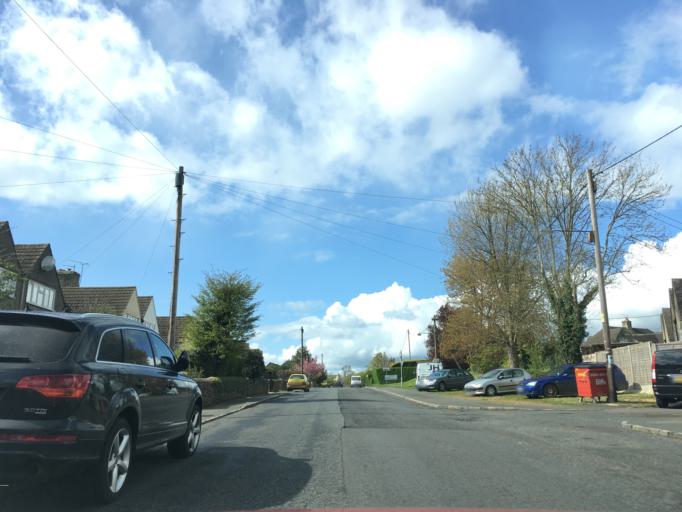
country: GB
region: England
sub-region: Gloucestershire
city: Tetbury
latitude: 51.6432
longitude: -2.1644
